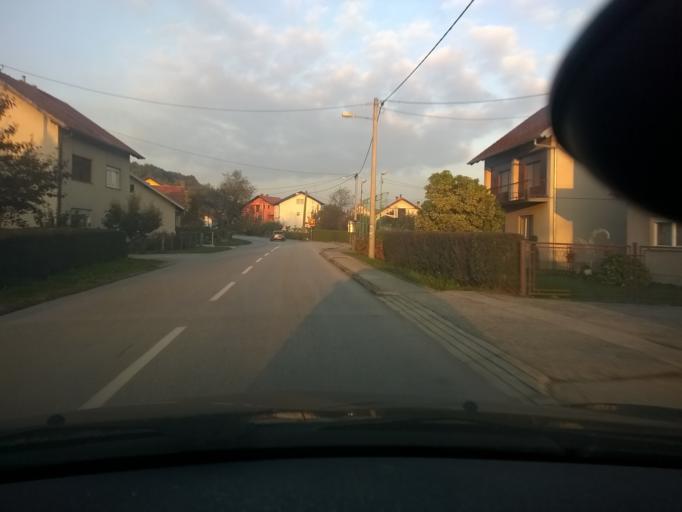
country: HR
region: Krapinsko-Zagorska
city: Zabok
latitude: 46.0173
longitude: 15.8828
